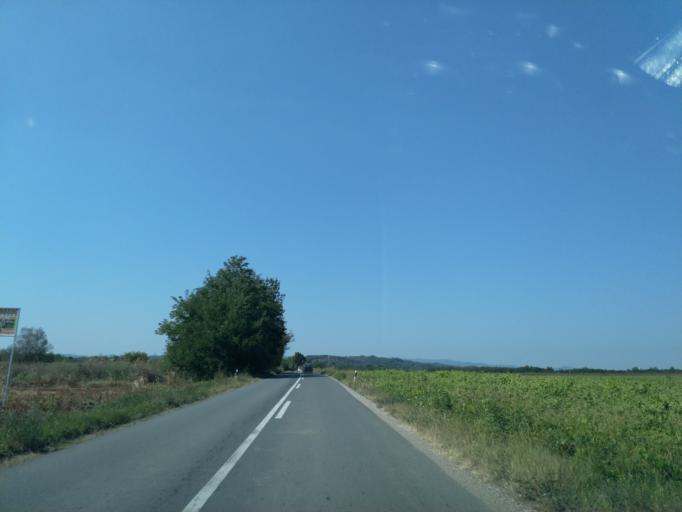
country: RS
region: Central Serbia
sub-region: Rasinski Okrug
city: Trstenik
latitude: 43.6279
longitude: 21.1560
